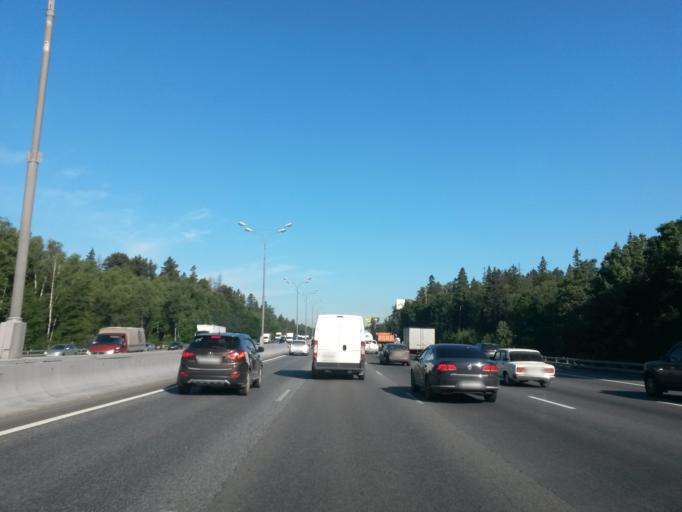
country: RU
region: Moscow
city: Gol'yanovo
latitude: 55.8487
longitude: 37.7918
